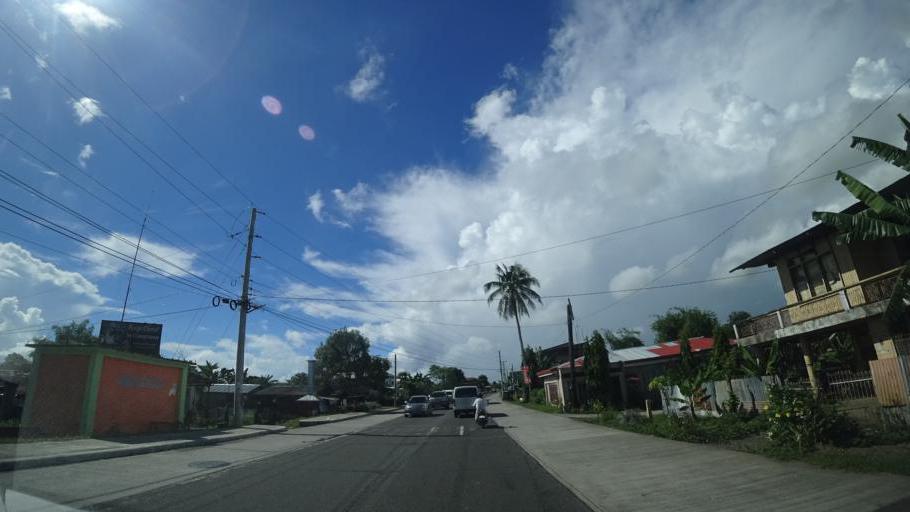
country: PH
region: Eastern Visayas
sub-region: Province of Leyte
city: Palo
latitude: 11.1409
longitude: 125.0049
